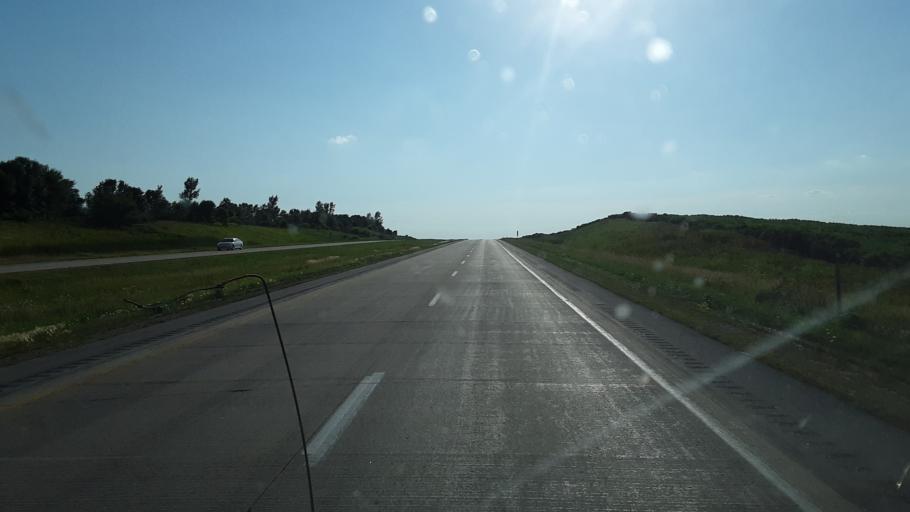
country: US
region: Iowa
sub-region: Hardin County
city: Iowa Falls
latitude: 42.4484
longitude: -93.3128
